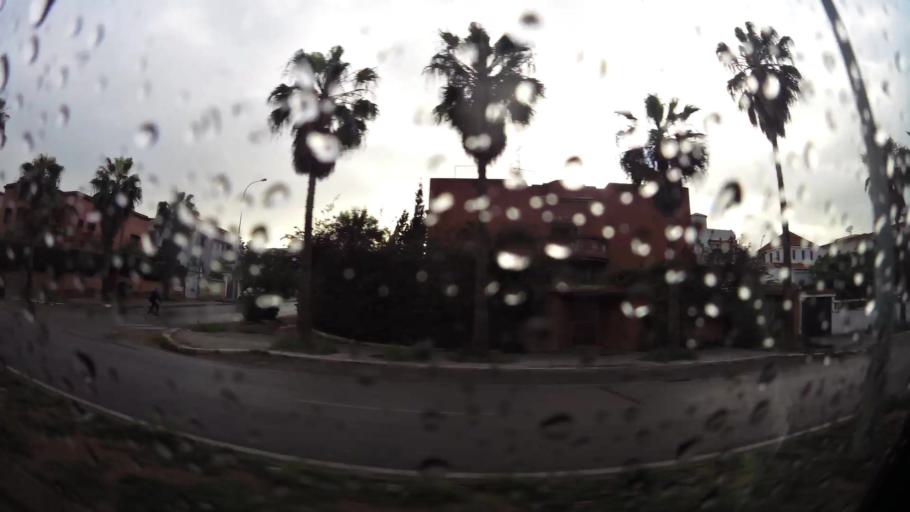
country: MA
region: Doukkala-Abda
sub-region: El-Jadida
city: El Jadida
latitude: 33.2301
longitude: -8.4934
